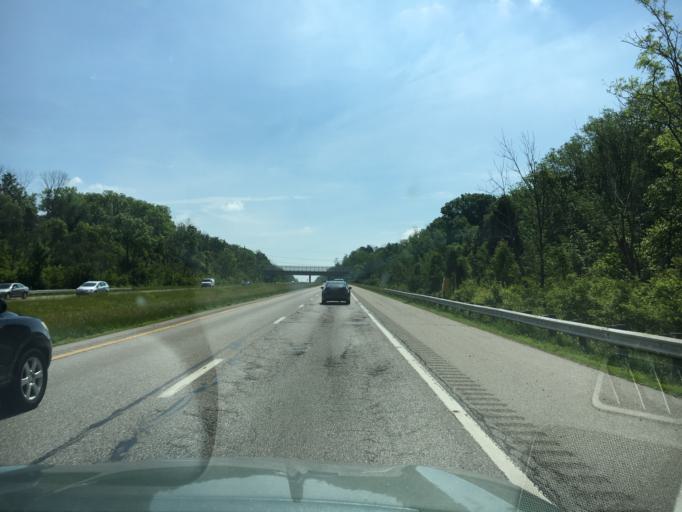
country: US
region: Ohio
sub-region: Hamilton County
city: Dent
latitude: 39.1868
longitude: -84.6323
